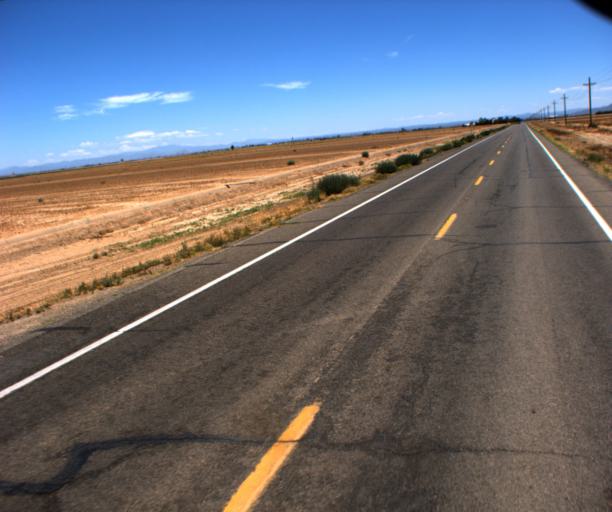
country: US
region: Arizona
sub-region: Pinal County
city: Coolidge
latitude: 32.8797
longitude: -111.6018
